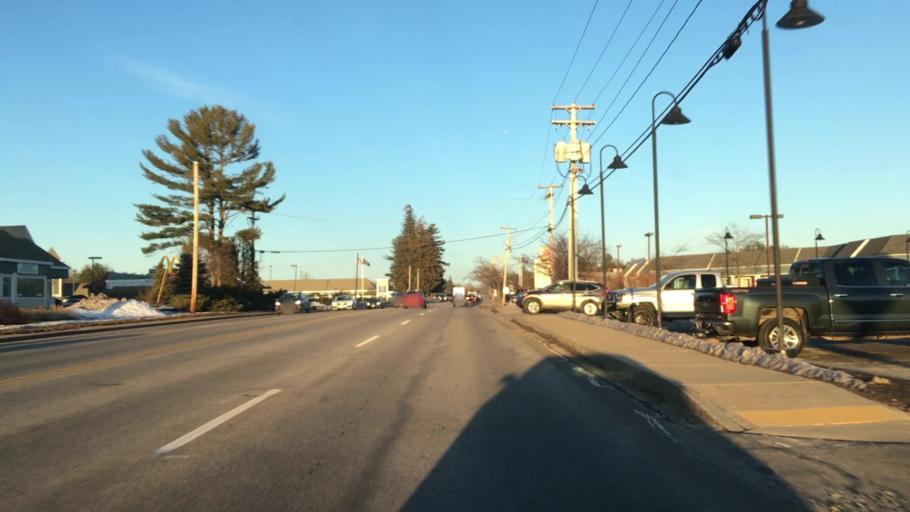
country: US
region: Maine
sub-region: York County
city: Kittery
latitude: 43.1136
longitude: -70.7318
